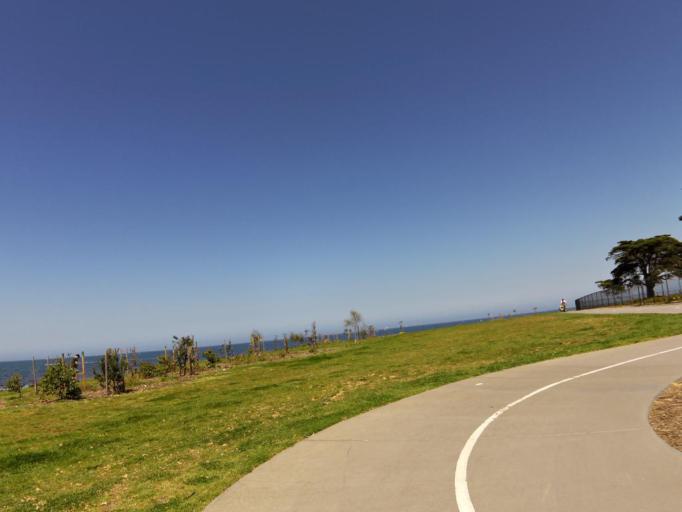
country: AU
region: Victoria
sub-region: Hobsons Bay
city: Williamstown
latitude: -37.8713
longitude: 144.9048
